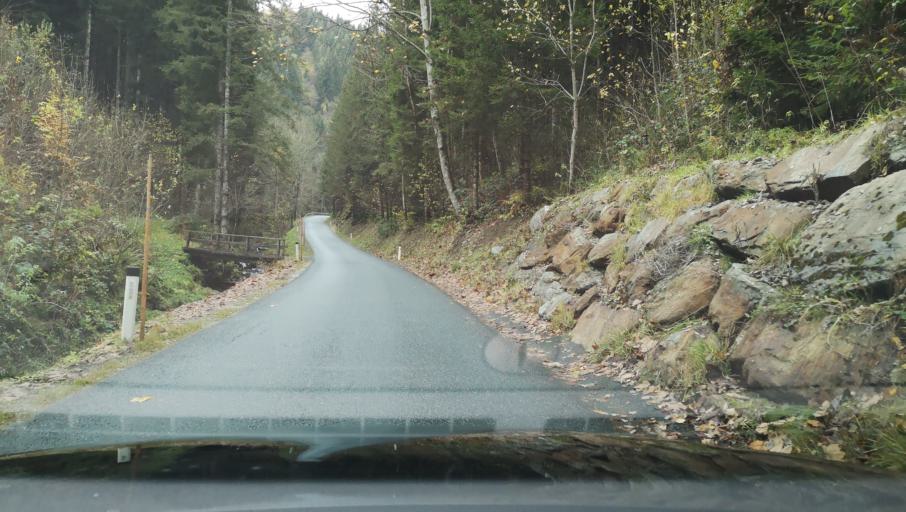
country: AT
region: Styria
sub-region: Politischer Bezirk Weiz
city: Birkfeld
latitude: 47.3647
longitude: 15.6353
